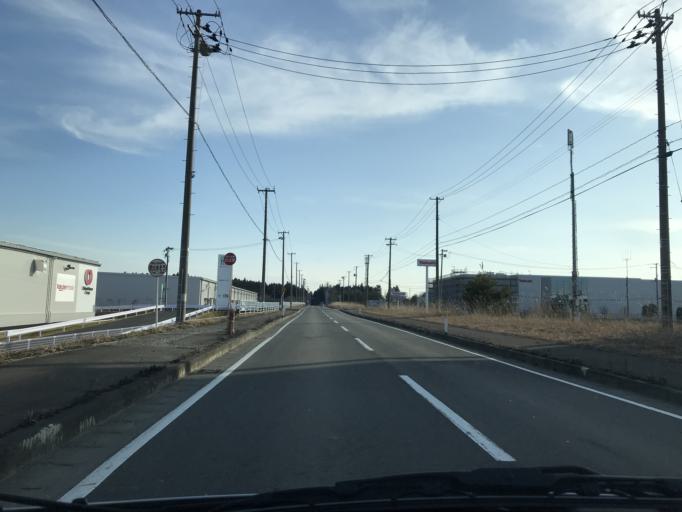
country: JP
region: Iwate
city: Kitakami
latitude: 39.2419
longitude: 141.0848
